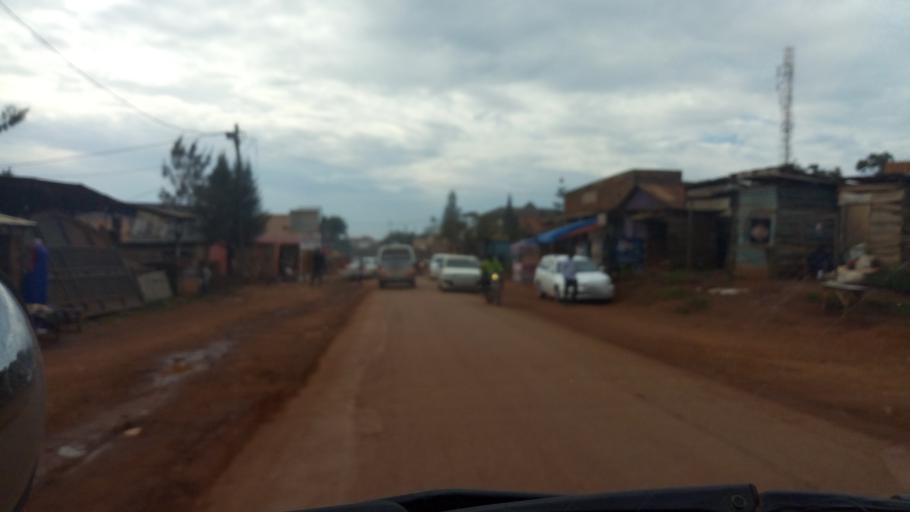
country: UG
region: Central Region
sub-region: Mukono District
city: Mukono
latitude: 0.3646
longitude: 32.7149
